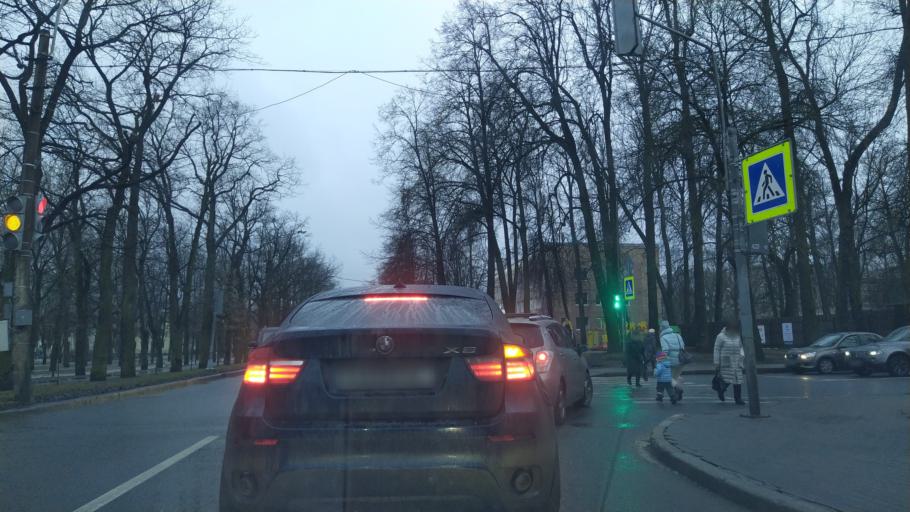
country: RU
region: St.-Petersburg
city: Pushkin
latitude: 59.7195
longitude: 30.4240
